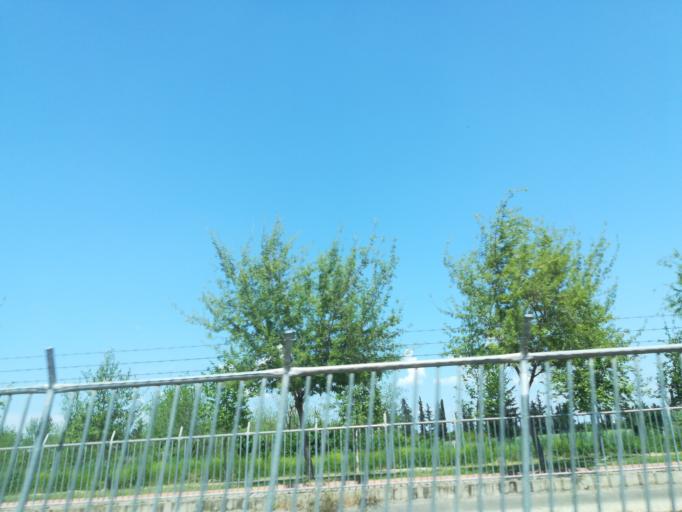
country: TR
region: Adana
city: Yuregir
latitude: 37.0196
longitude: 35.3730
